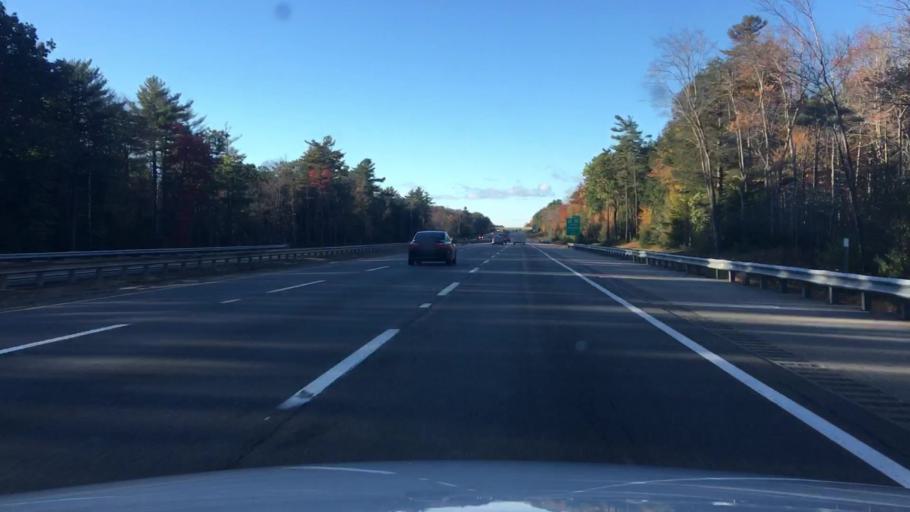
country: US
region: Maine
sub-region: York County
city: Wells Beach Station
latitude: 43.3446
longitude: -70.5964
